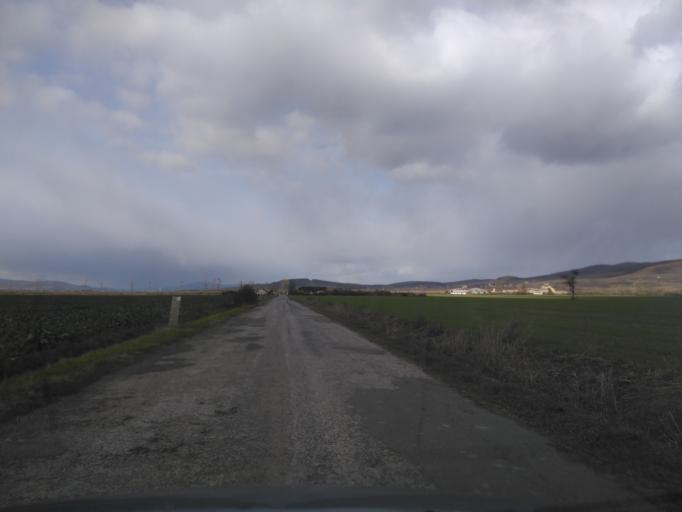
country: HU
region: Borsod-Abauj-Zemplen
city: Satoraljaujhely
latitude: 48.4171
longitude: 21.6784
